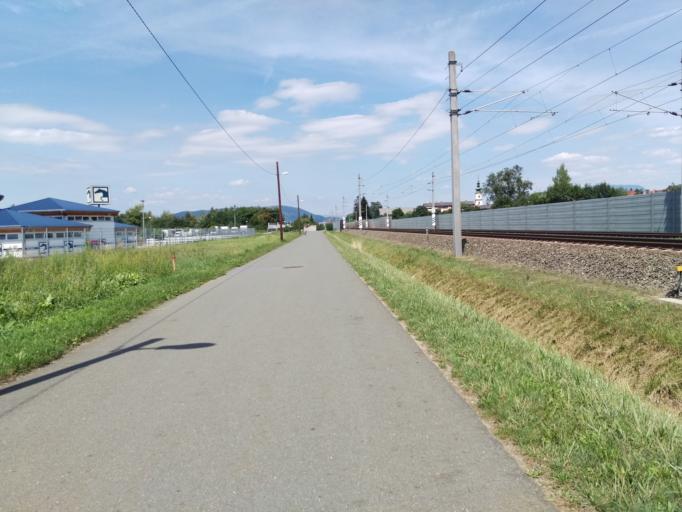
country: AT
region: Styria
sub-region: Politischer Bezirk Graz-Umgebung
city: Feldkirchen bei Graz
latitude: 47.0077
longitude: 15.4433
